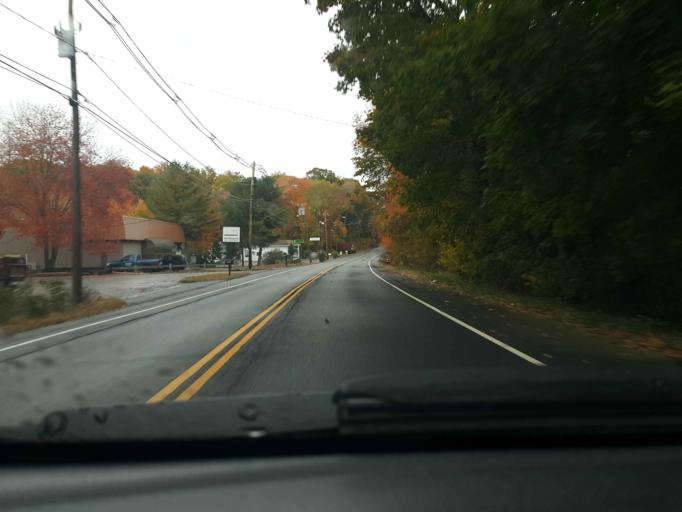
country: US
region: Connecticut
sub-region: New Haven County
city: Madison
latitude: 41.2774
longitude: -72.5821
